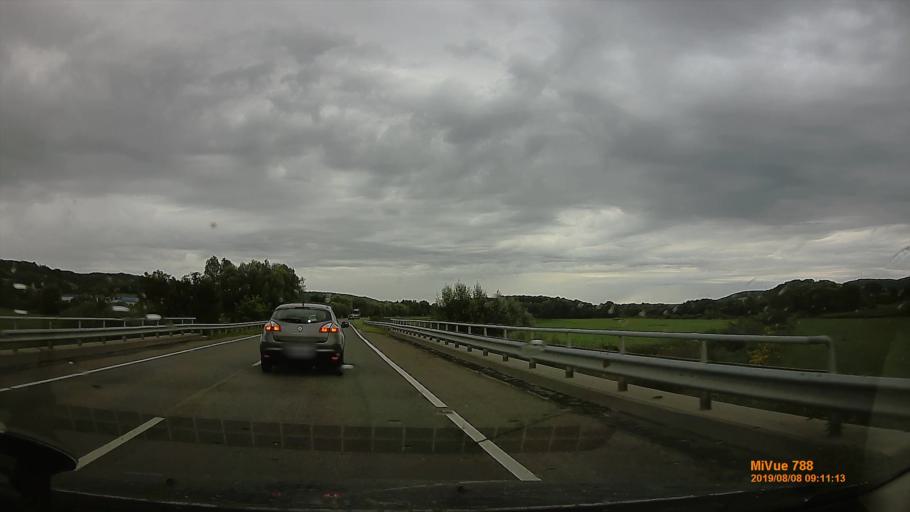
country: HU
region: Zala
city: Zalaegerszeg
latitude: 46.7806
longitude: 16.8566
